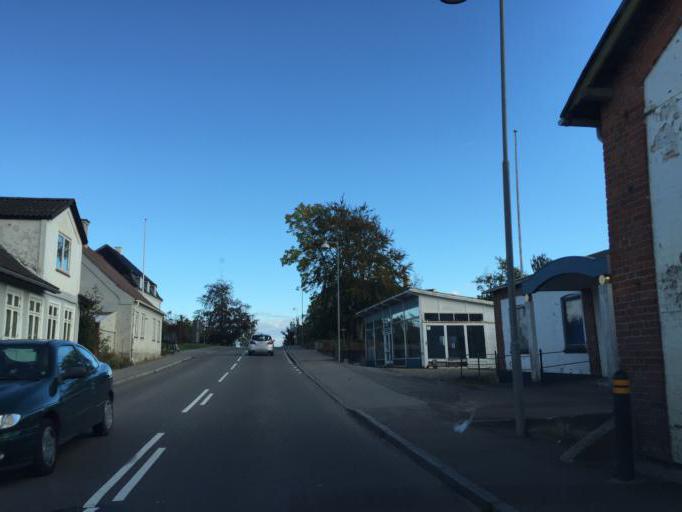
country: DK
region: Zealand
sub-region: Odsherred Kommune
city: Asnaes
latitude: 55.8099
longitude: 11.5040
